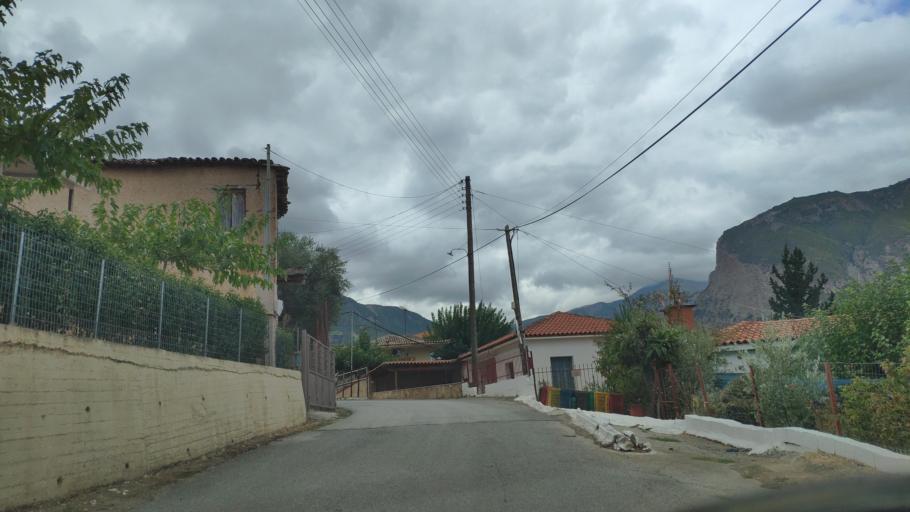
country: GR
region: West Greece
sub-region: Nomos Achaias
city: Temeni
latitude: 38.1779
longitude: 22.1451
